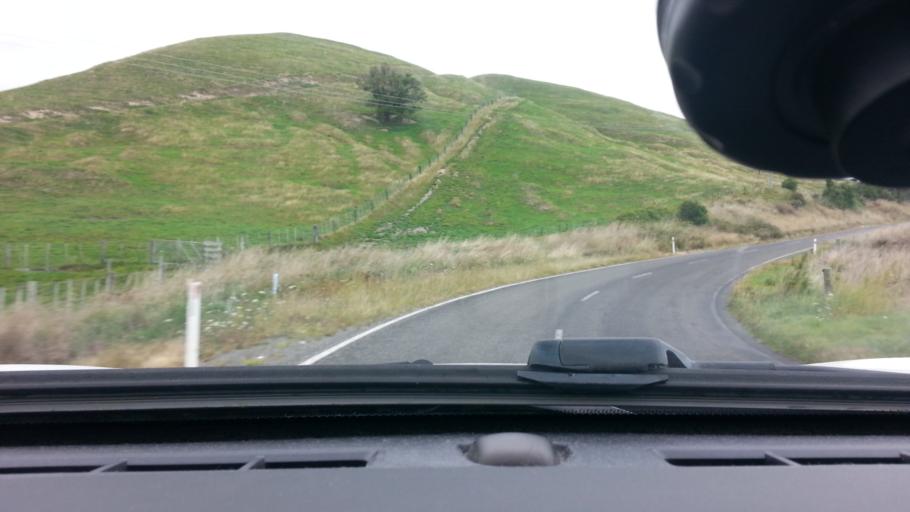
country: NZ
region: Wellington
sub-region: South Wairarapa District
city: Waipawa
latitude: -41.4256
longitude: 175.2254
